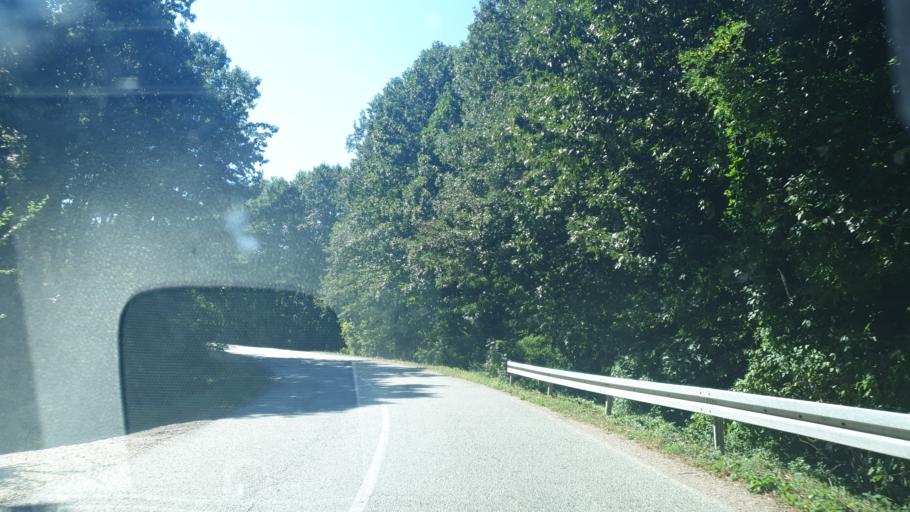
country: RS
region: Central Serbia
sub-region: Kolubarski Okrug
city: Mionica
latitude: 44.2139
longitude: 20.0812
